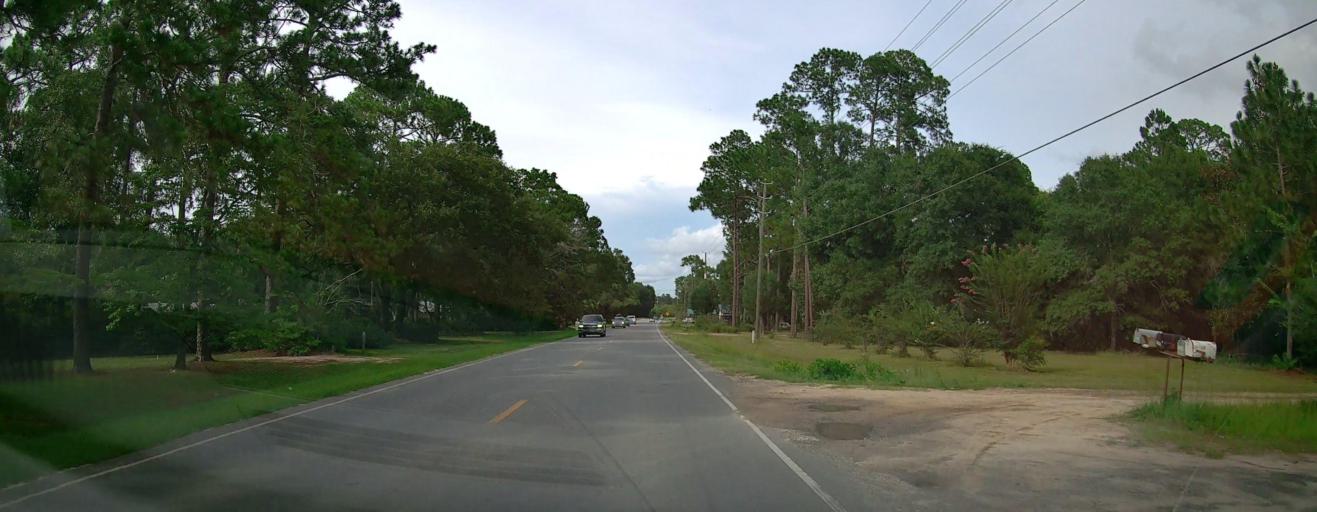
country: US
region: Georgia
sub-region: Wayne County
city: Jesup
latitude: 31.6594
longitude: -81.8893
